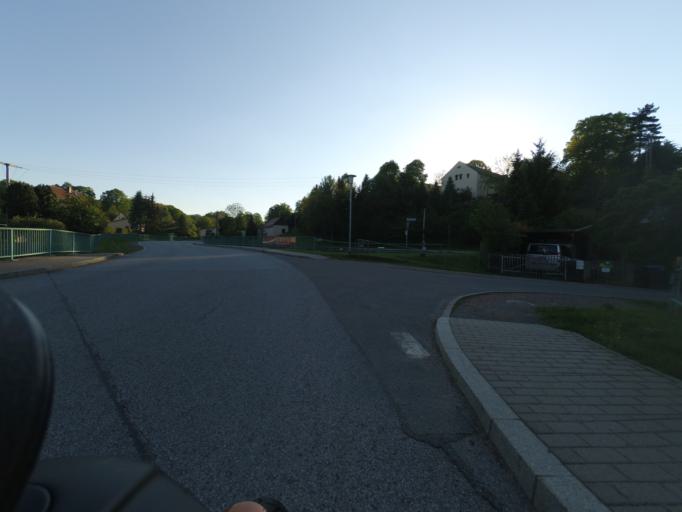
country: DE
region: Saxony
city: Reinhardtsgrimma
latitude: 50.8912
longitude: 13.7494
